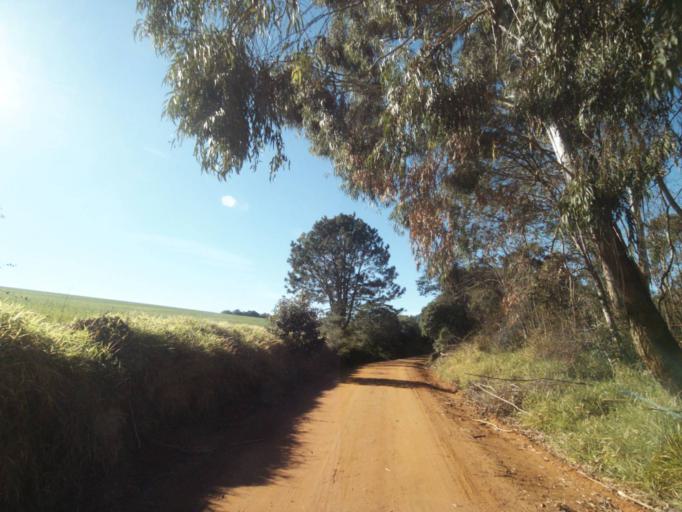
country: BR
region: Parana
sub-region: Tibagi
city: Tibagi
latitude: -24.5357
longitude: -50.3725
